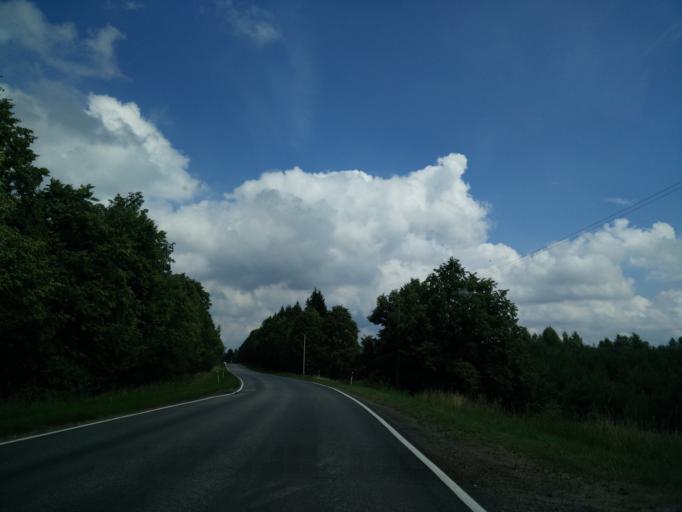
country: LT
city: Skaidiskes
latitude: 54.6915
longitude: 25.4673
